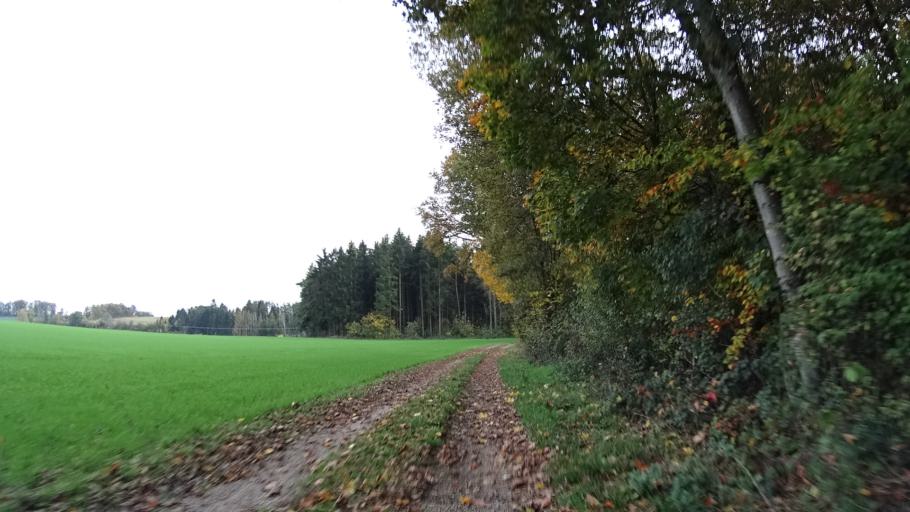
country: DE
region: Bavaria
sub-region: Upper Bavaria
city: Hitzhofen
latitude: 48.8429
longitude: 11.3027
